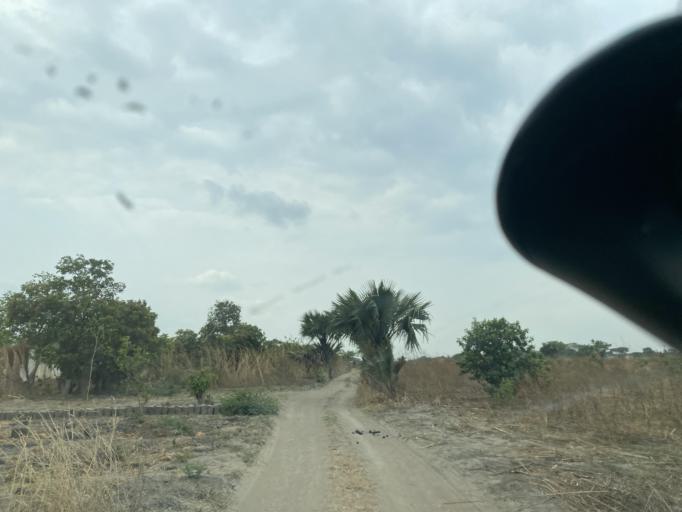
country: ZM
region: Lusaka
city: Lusaka
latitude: -15.2325
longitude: 28.3352
